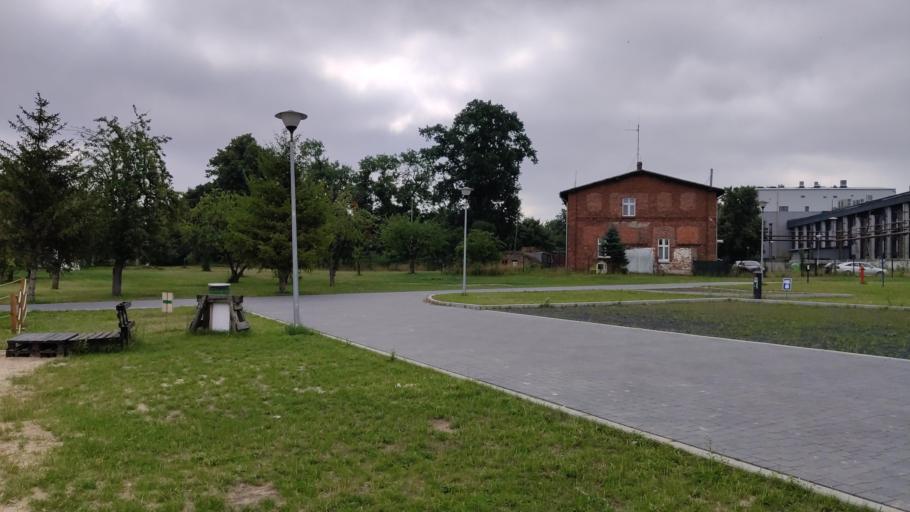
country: PL
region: Kujawsko-Pomorskie
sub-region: Powiat zninski
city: Znin
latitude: 52.8519
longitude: 17.7372
